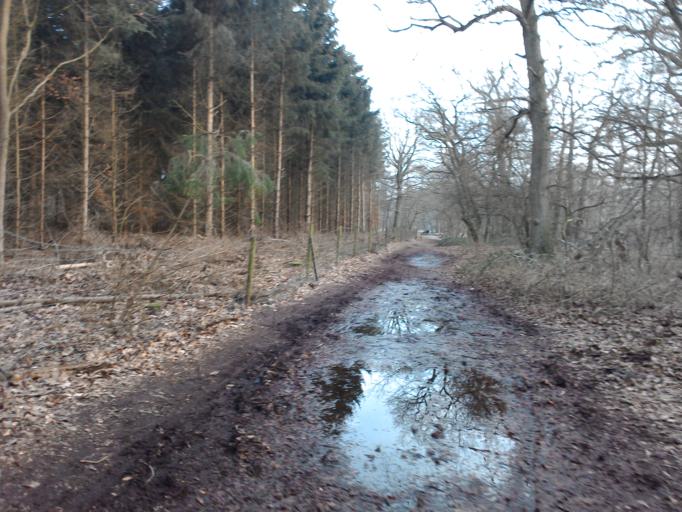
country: NL
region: Utrecht
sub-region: Gemeente De Bilt
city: De Bilt
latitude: 52.1137
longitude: 5.2022
